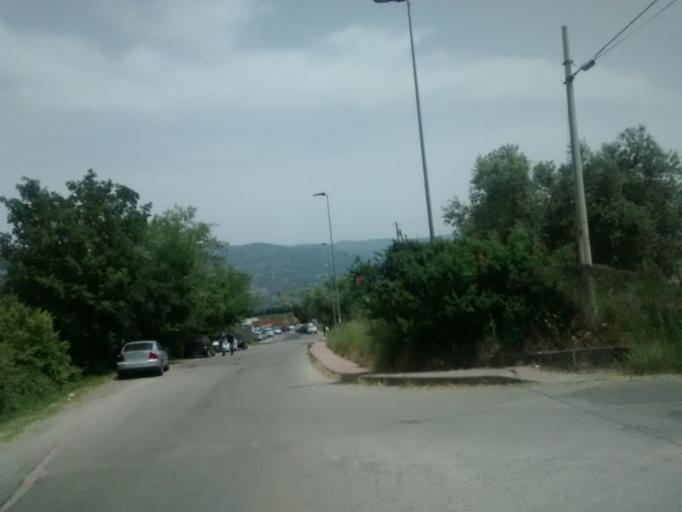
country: IT
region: Calabria
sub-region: Provincia di Cosenza
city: Arcavacata
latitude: 39.3639
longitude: 16.2234
